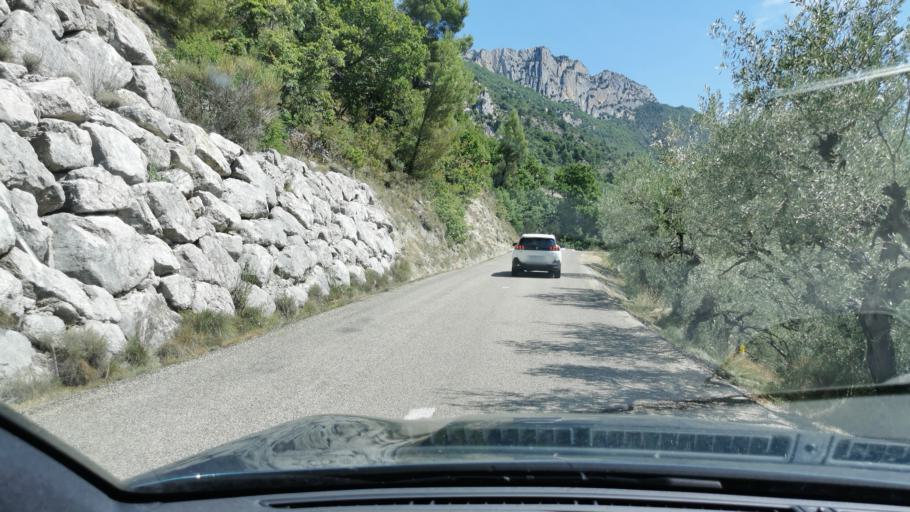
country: FR
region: Rhone-Alpes
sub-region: Departement de la Drome
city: Buis-les-Baronnies
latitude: 44.3005
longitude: 5.2875
